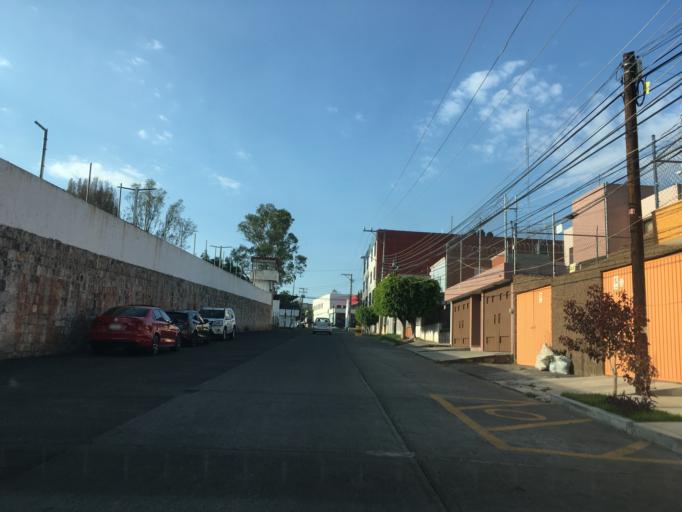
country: MX
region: Michoacan
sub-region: Morelia
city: Puerto de Buenavista (Lazaro Cardenas)
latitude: 19.6937
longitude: -101.1511
